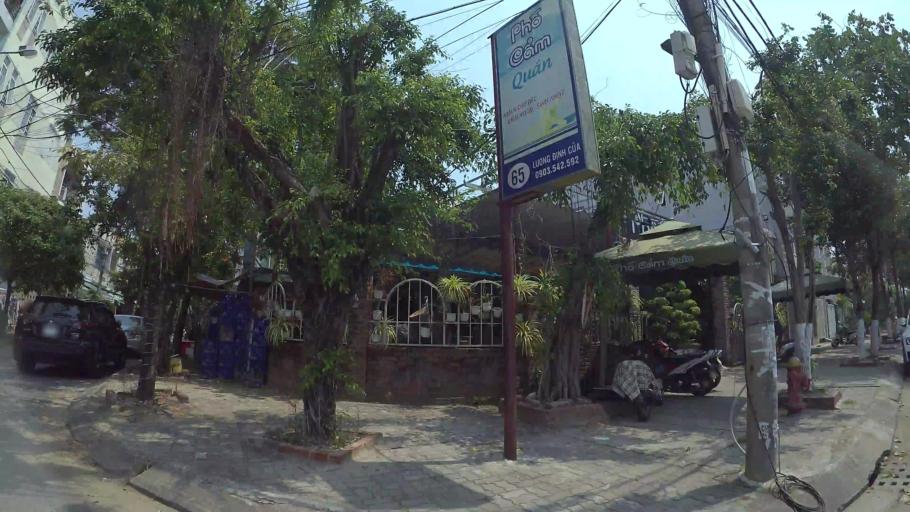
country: VN
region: Da Nang
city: Cam Le
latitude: 16.0160
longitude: 108.2093
